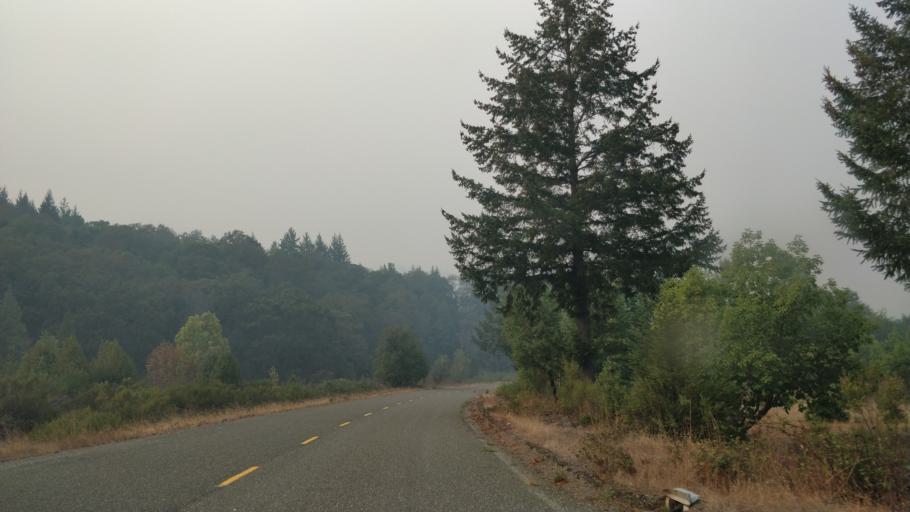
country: US
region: California
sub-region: Humboldt County
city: Rio Dell
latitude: 40.3364
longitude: -124.0270
